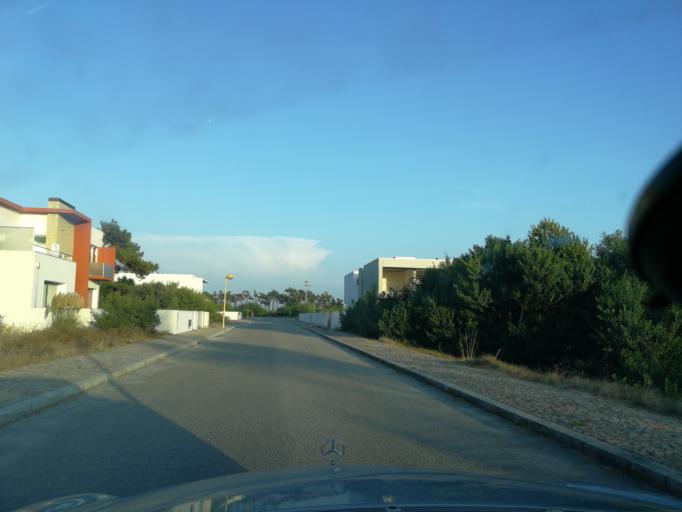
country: PT
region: Aveiro
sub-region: Murtosa
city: Murtosa
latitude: 40.7560
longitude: -8.7075
